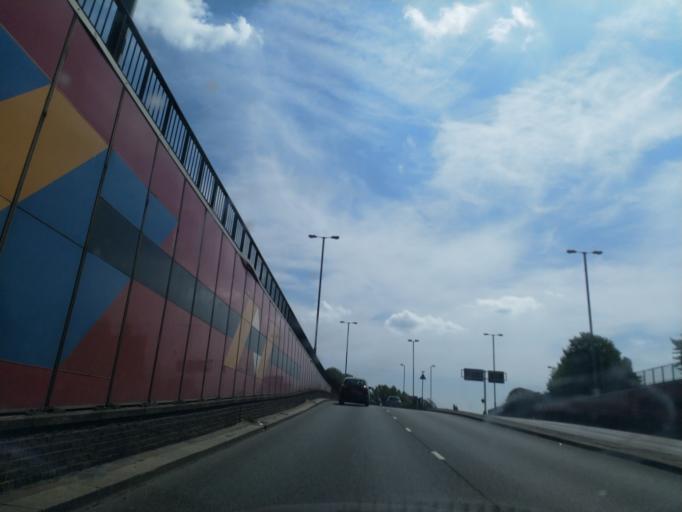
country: GB
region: England
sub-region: City and Borough of Birmingham
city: Hockley
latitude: 52.5019
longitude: -1.8979
